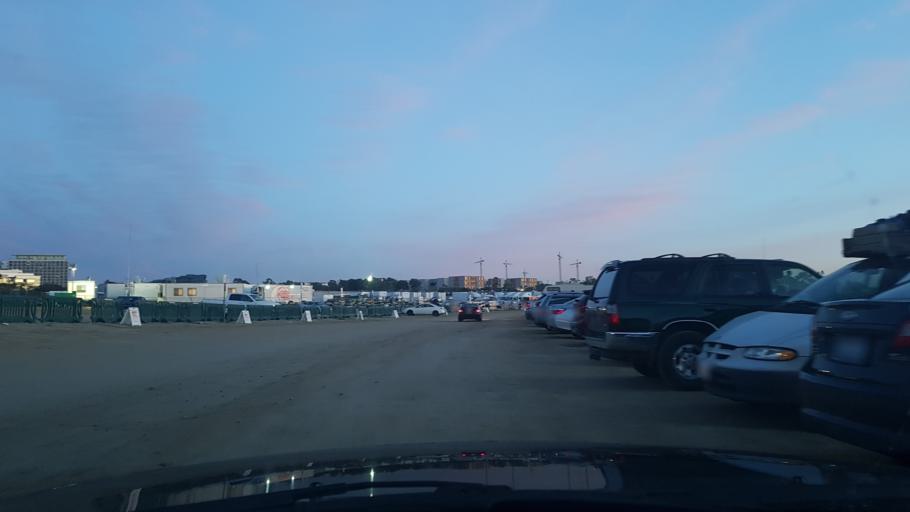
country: US
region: California
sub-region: San Diego County
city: La Jolla
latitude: 32.8913
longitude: -117.2500
